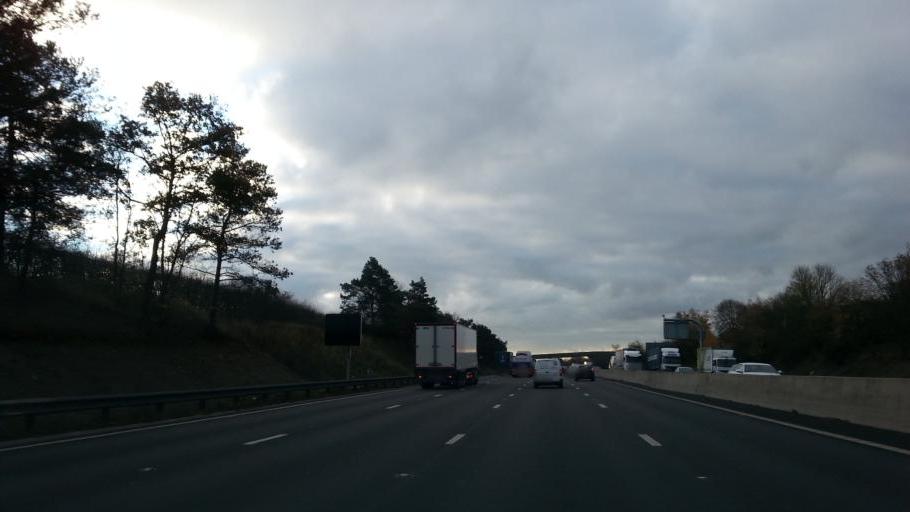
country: GB
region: England
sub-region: Northamptonshire
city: Long Buckby
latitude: 52.2991
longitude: -1.1154
